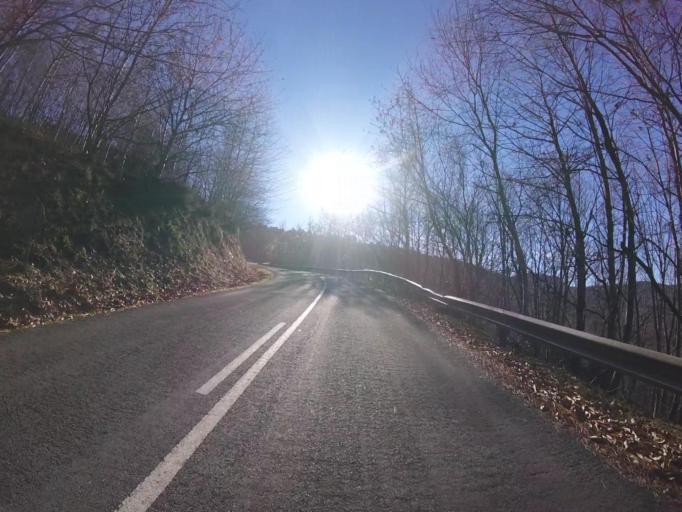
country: ES
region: Basque Country
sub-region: Provincia de Guipuzcoa
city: Irun
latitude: 43.3138
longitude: -1.7584
